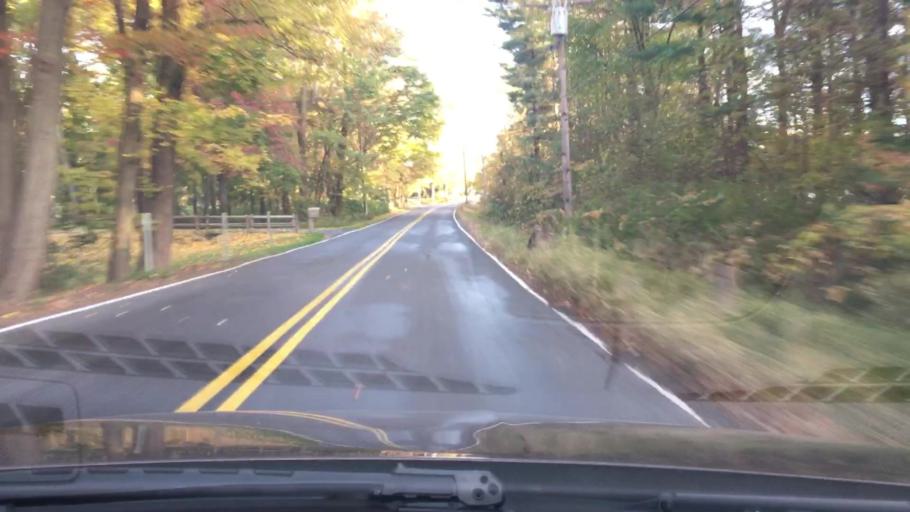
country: US
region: Connecticut
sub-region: Tolland County
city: Somers
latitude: 42.0086
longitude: -72.4811
